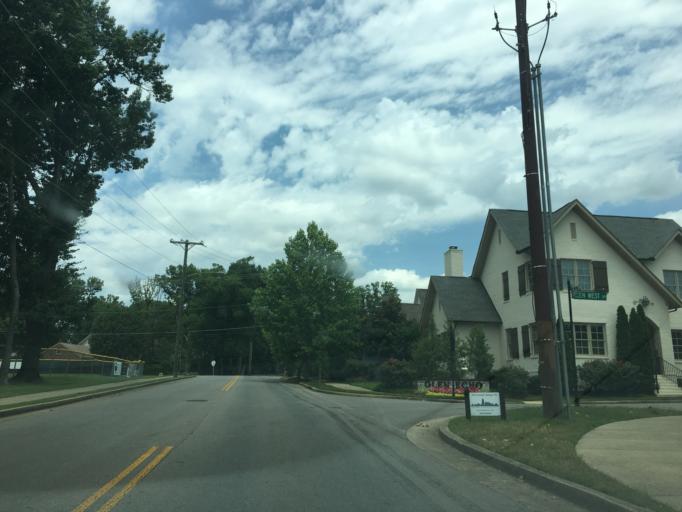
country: US
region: Tennessee
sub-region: Davidson County
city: Oak Hill
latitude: 36.1068
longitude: -86.8080
